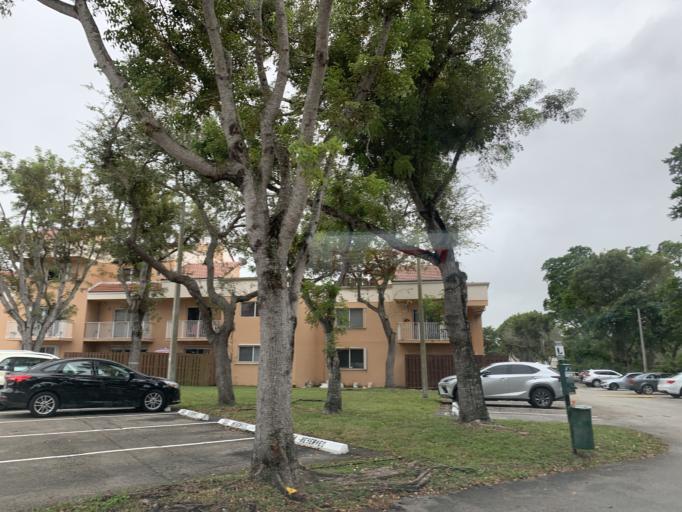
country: US
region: Florida
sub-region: Miami-Dade County
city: Kendall West
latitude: 25.6936
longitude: -80.4355
